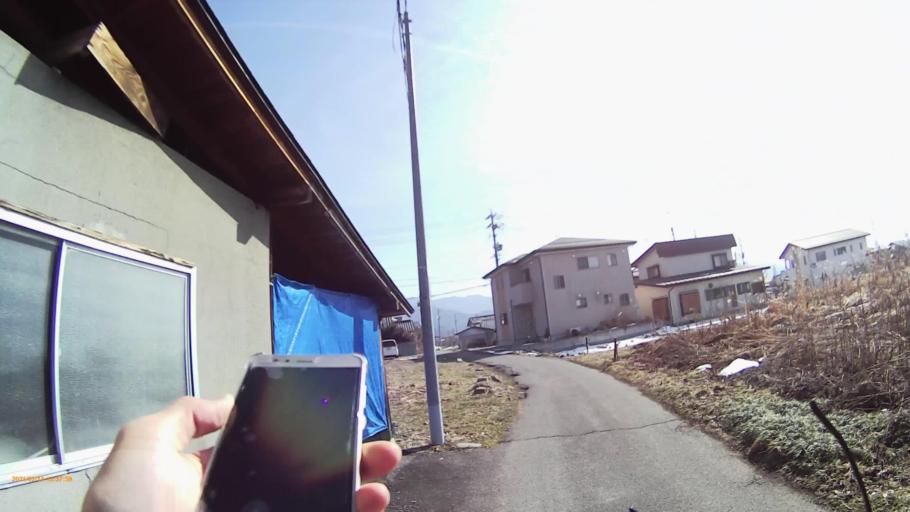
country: JP
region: Nagano
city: Nakano
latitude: 36.7549
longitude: 138.3737
